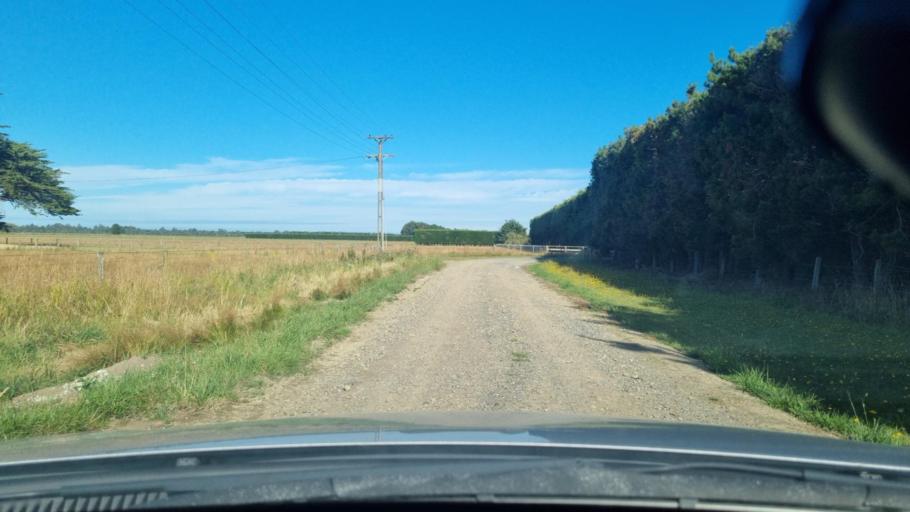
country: NZ
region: Southland
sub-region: Invercargill City
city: Invercargill
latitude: -46.3605
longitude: 168.3016
